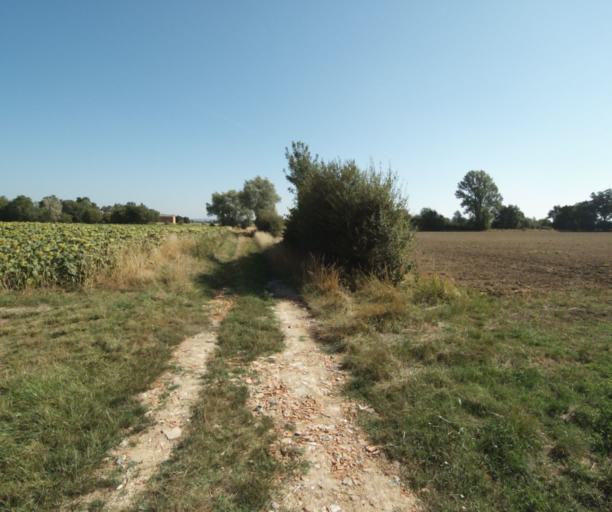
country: FR
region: Midi-Pyrenees
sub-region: Departement de la Haute-Garonne
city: Revel
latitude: 43.4723
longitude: 1.9587
